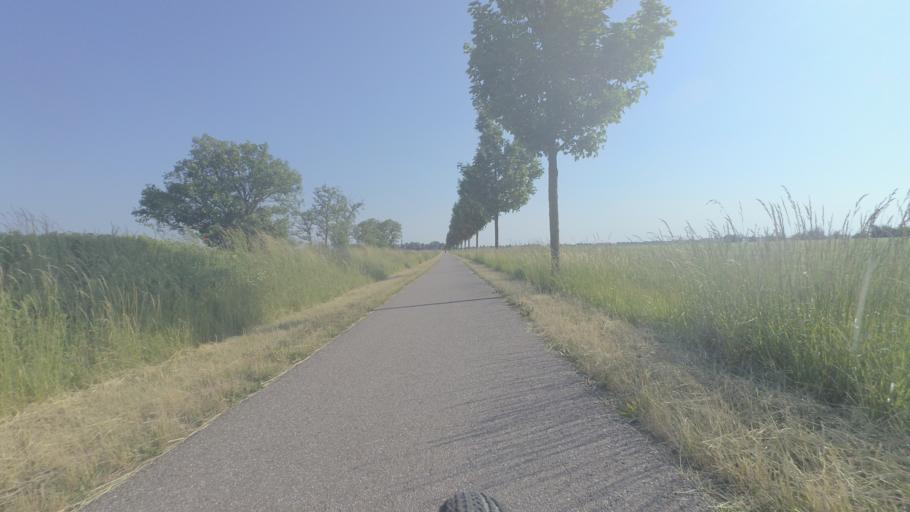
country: DE
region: Saxony-Anhalt
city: Osternienburger Land
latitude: 51.7833
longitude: 12.0068
